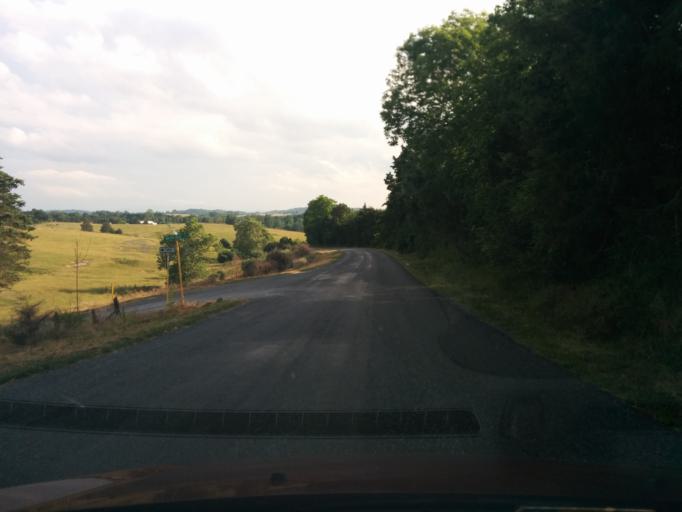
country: US
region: Virginia
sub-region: Rockbridge County
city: East Lexington
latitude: 37.8053
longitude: -79.4031
